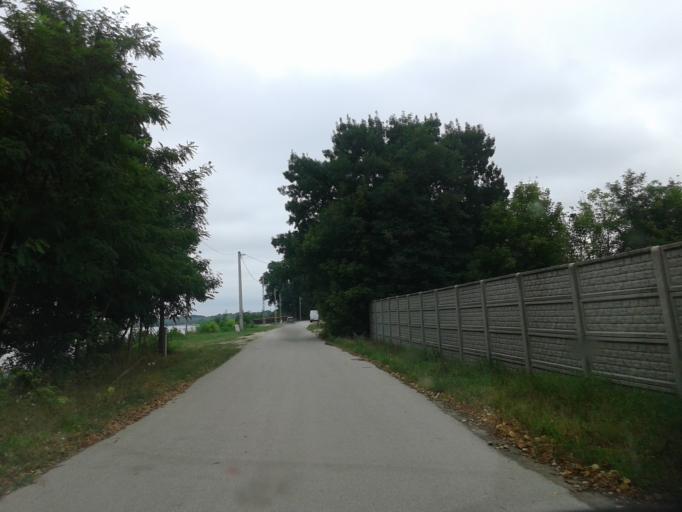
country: HU
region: Bacs-Kiskun
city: Harta
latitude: 46.6971
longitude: 19.0117
